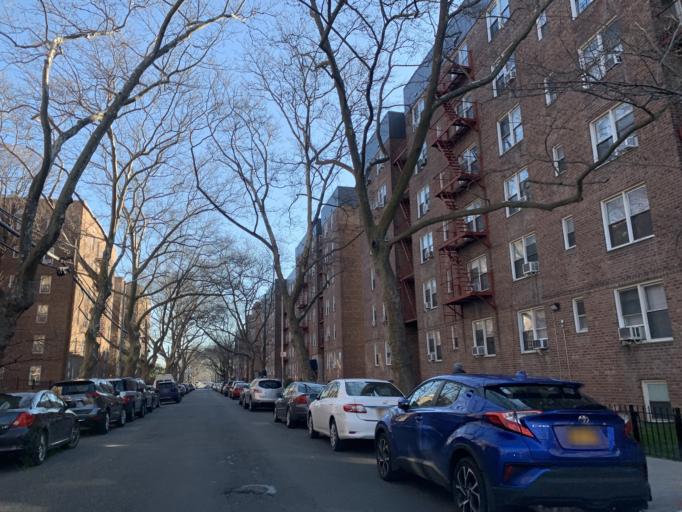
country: US
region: New York
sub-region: Queens County
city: Borough of Queens
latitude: 40.7310
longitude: -73.8511
